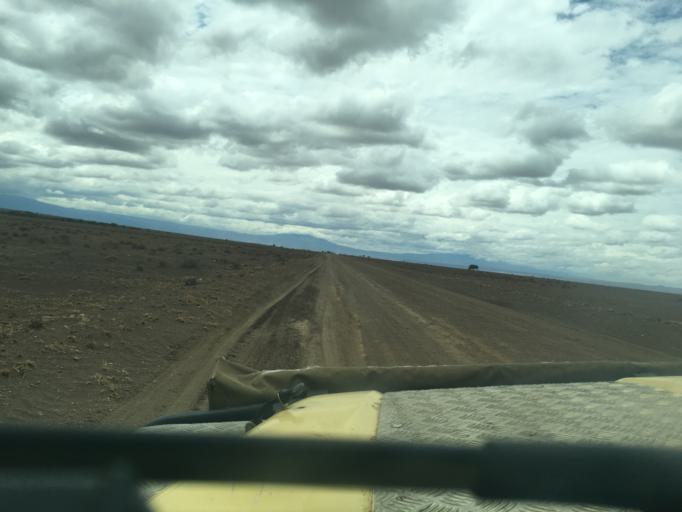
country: TZ
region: Arusha
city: Mto wa Mbu
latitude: -2.9009
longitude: 36.0592
